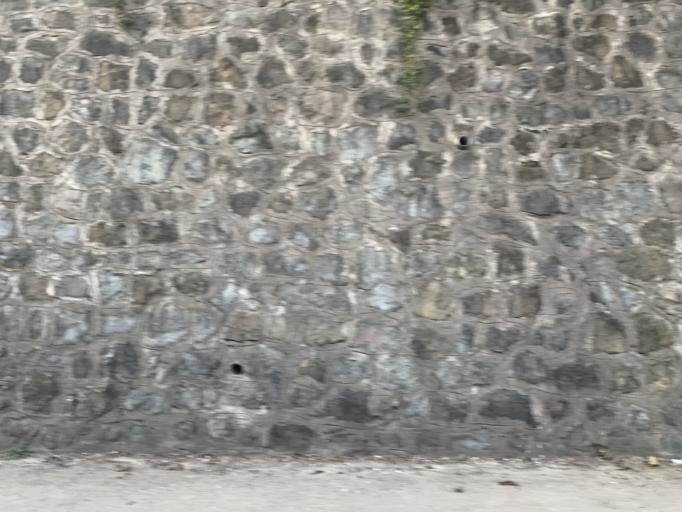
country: TR
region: Trabzon
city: Dernekpazari
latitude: 40.8306
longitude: 40.2692
